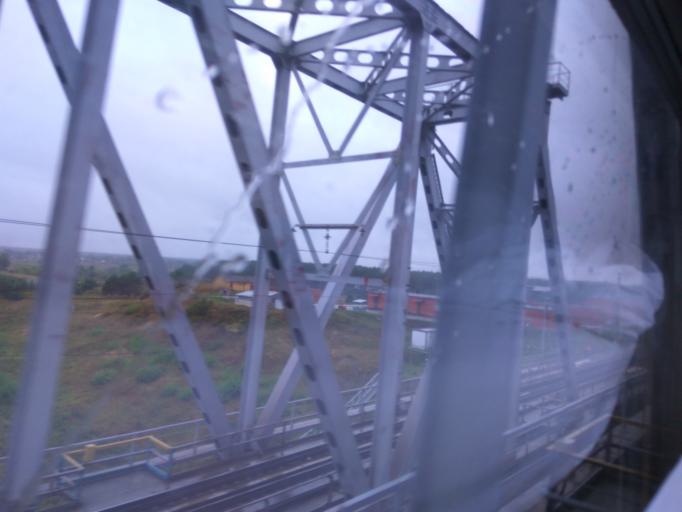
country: RU
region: Moskovskaya
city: Kashira
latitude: 54.8630
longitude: 38.1630
